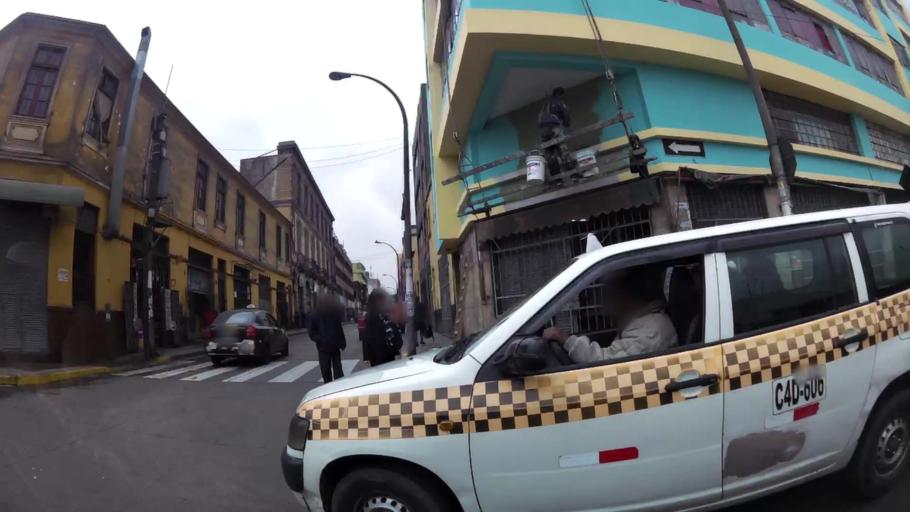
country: PE
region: Lima
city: Lima
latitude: -12.0444
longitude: -77.0388
